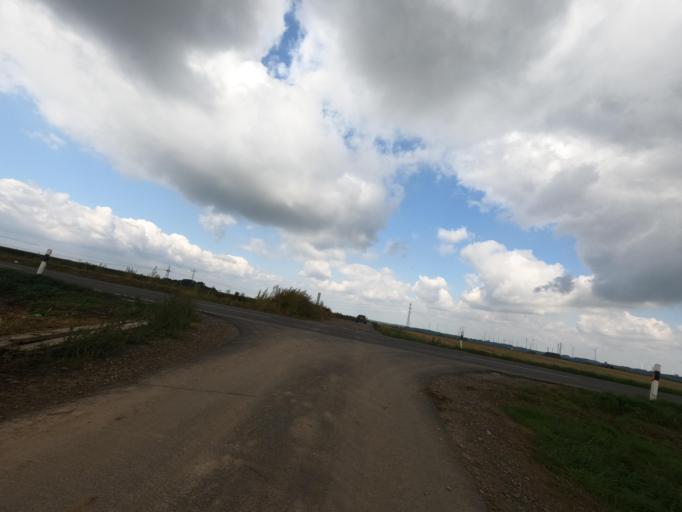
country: DE
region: North Rhine-Westphalia
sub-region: Regierungsbezirk Koln
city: Linnich
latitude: 50.9840
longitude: 6.2451
